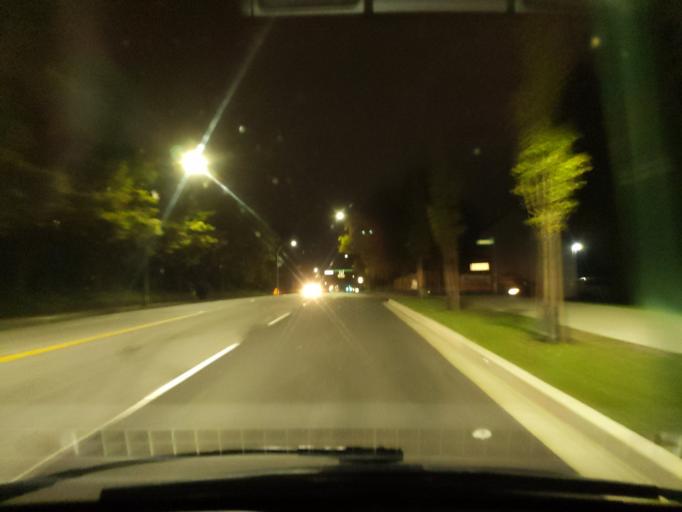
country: CA
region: British Columbia
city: Burnaby
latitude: 49.2547
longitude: -123.0134
